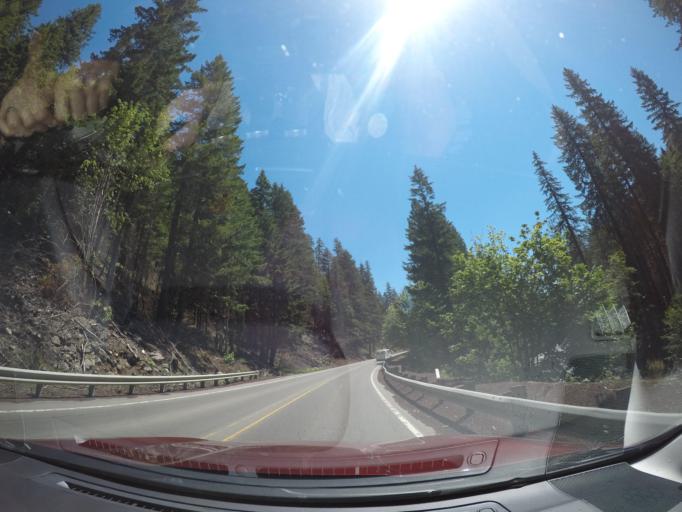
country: US
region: Oregon
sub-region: Linn County
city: Mill City
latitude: 44.6940
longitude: -121.9809
